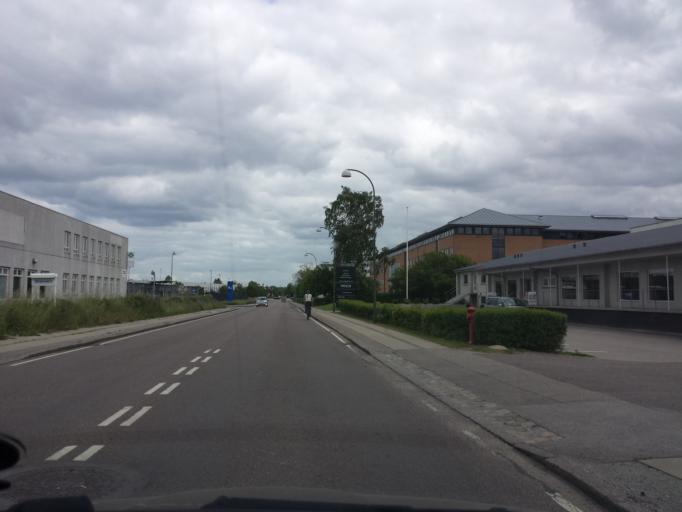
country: DK
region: Capital Region
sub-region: Herlev Kommune
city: Herlev
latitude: 55.7165
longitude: 12.4305
